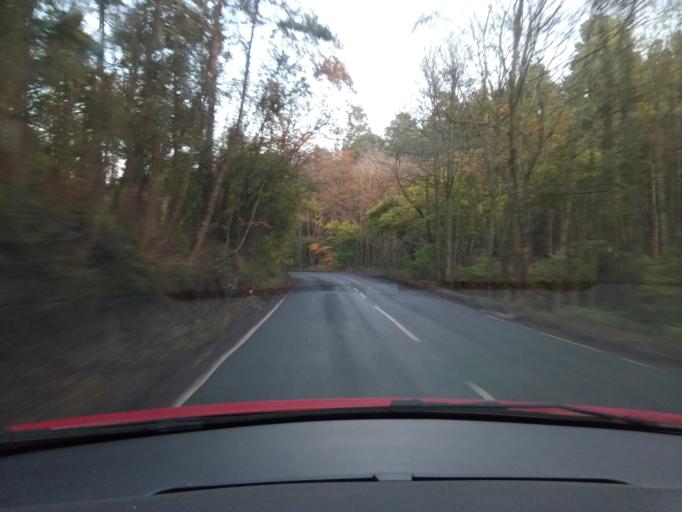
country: GB
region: England
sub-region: Northumberland
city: Bardon Mill
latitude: 54.9503
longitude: -2.2672
